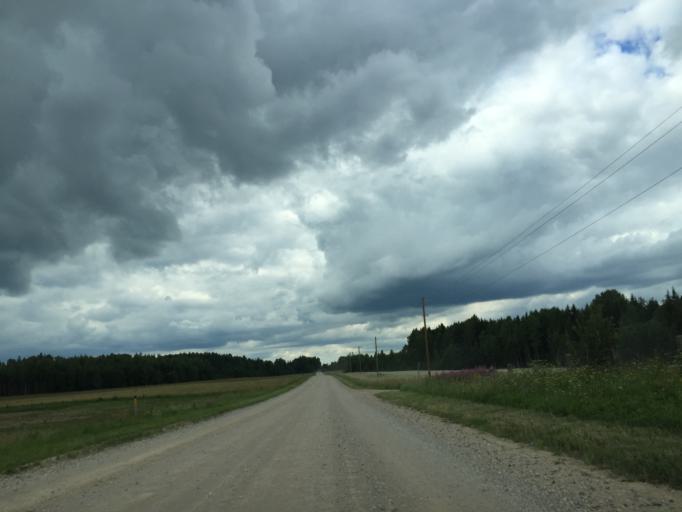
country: LV
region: Malpils
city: Malpils
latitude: 56.8649
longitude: 25.0134
